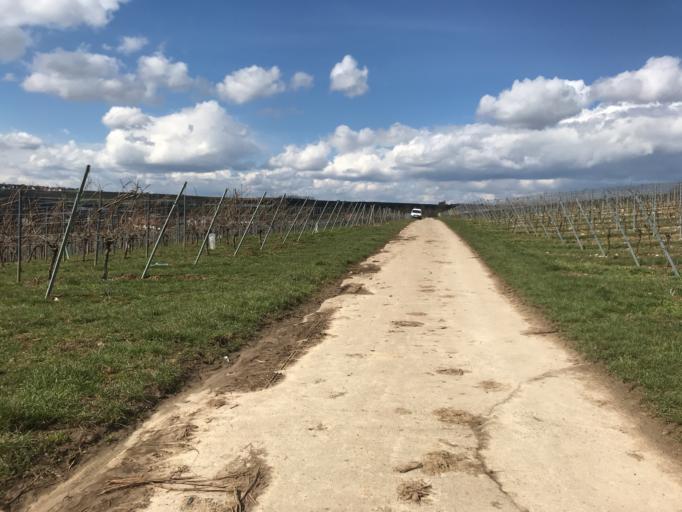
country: DE
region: Rheinland-Pfalz
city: Klein-Winternheim
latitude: 49.9353
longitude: 8.2254
